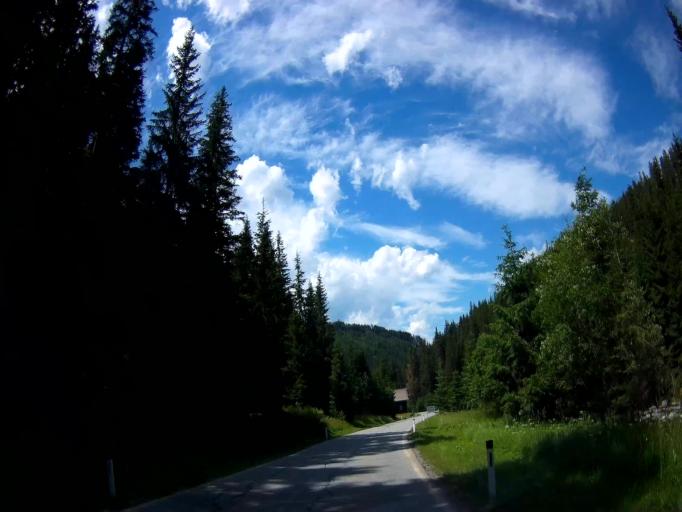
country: AT
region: Styria
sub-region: Politischer Bezirk Murau
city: Stadl an der Mur
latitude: 47.0142
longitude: 14.0061
